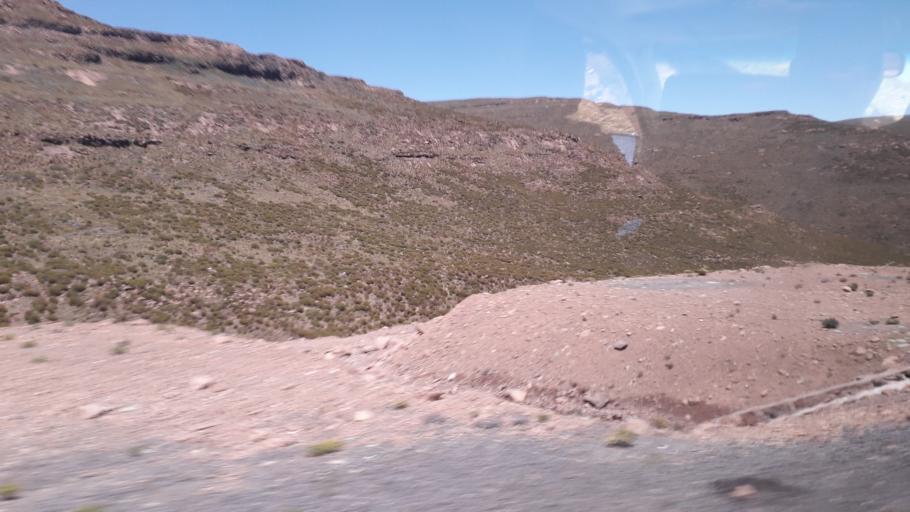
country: ZA
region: Orange Free State
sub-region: Thabo Mofutsanyana District Municipality
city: Phuthaditjhaba
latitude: -28.8049
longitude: 28.6965
